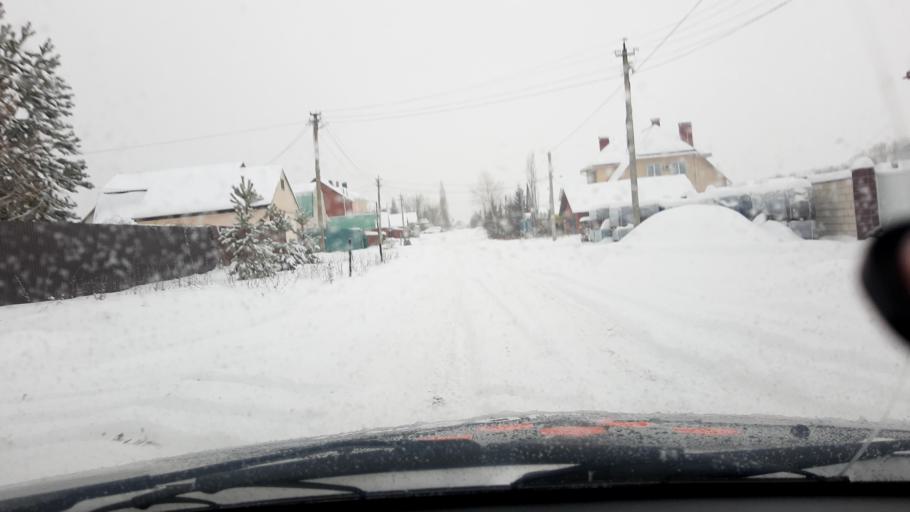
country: RU
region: Bashkortostan
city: Ufa
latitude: 54.6065
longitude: 55.9528
